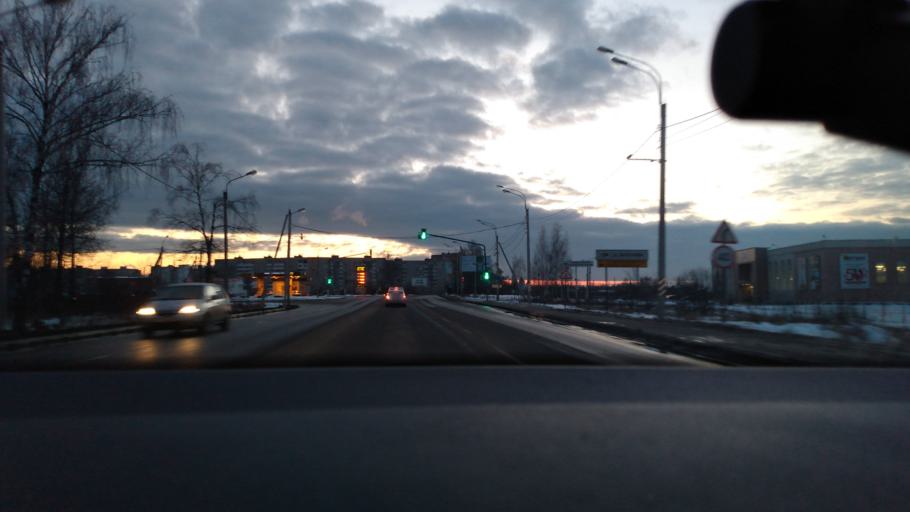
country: RU
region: Moskovskaya
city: Yegor'yevsk
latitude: 55.3839
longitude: 39.0667
